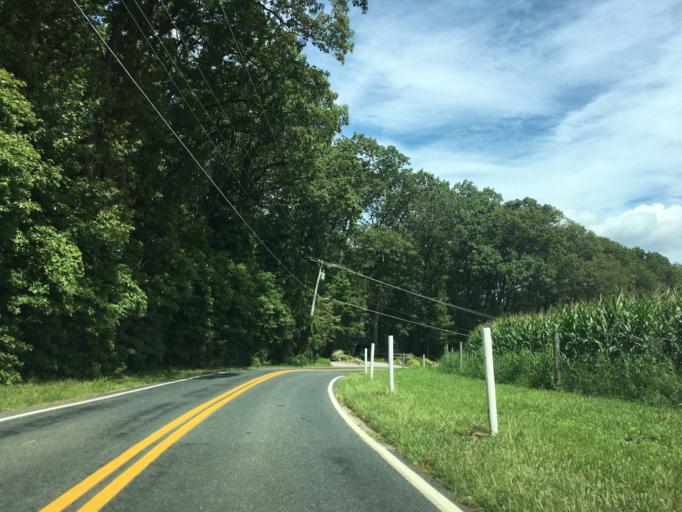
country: US
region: Pennsylvania
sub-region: York County
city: New Freedom
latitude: 39.7009
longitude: -76.6926
